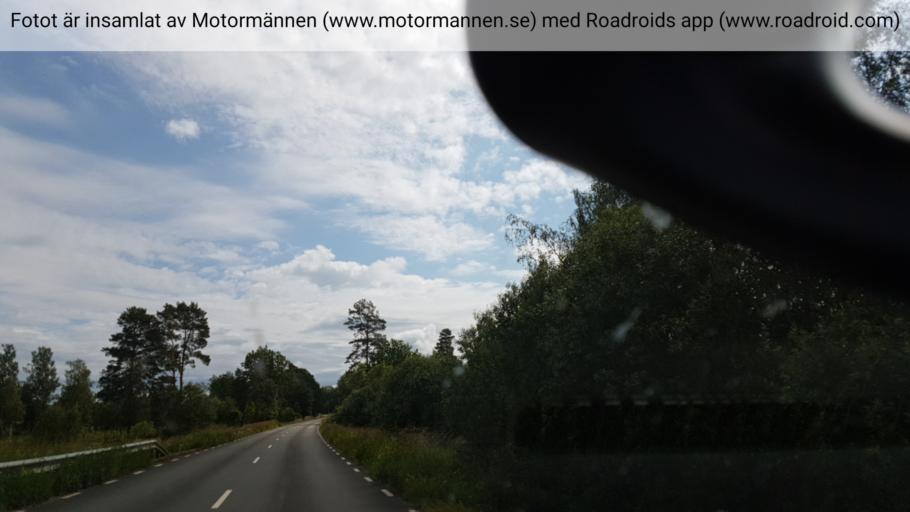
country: SE
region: Vaestra Goetaland
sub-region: Falkopings Kommun
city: Floby
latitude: 58.2102
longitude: 13.3814
